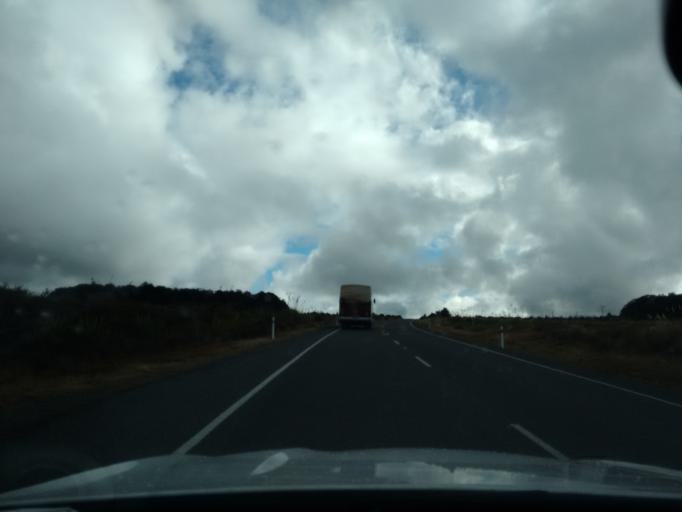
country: NZ
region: Manawatu-Wanganui
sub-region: Ruapehu District
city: Waiouru
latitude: -39.1782
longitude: 175.4662
